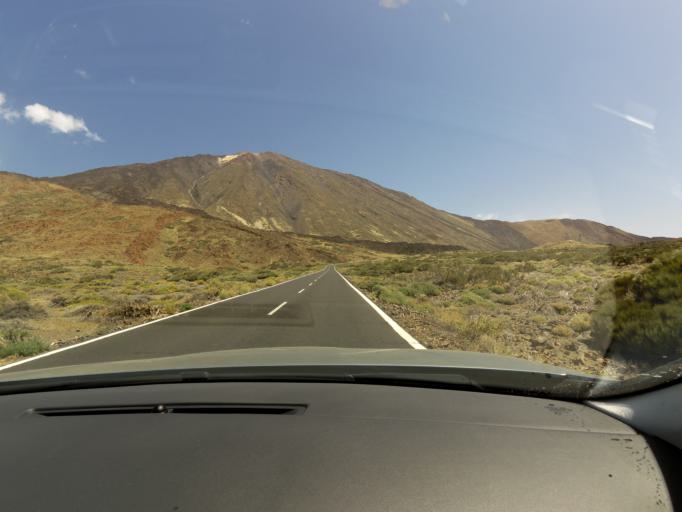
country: ES
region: Canary Islands
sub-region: Provincia de Santa Cruz de Tenerife
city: Vilaflor
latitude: 28.2405
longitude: -16.6300
